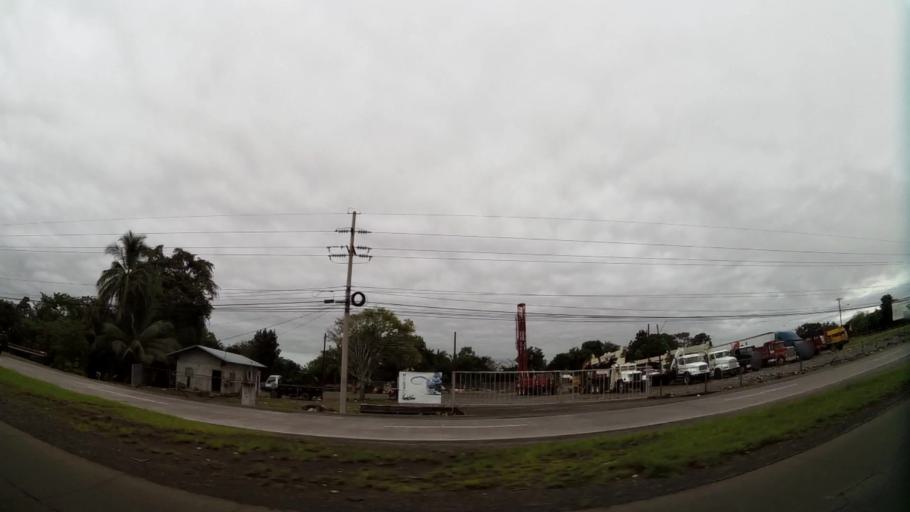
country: PA
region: Chiriqui
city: Boqueron
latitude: 8.4907
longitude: -82.5774
